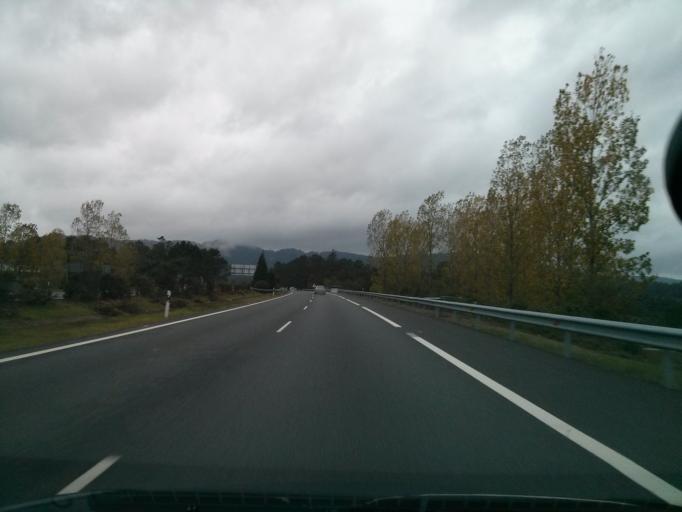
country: ES
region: Galicia
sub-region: Provincia de Pontevedra
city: Ponteareas
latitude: 42.1558
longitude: -8.4995
